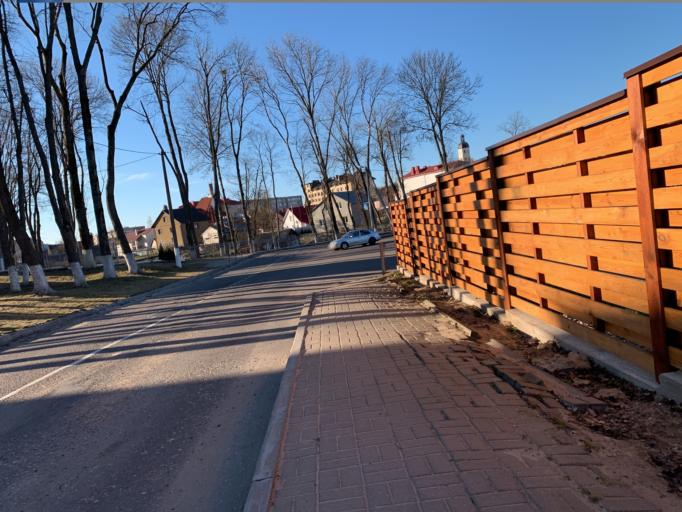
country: BY
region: Minsk
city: Nyasvizh
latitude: 53.2161
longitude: 26.6824
